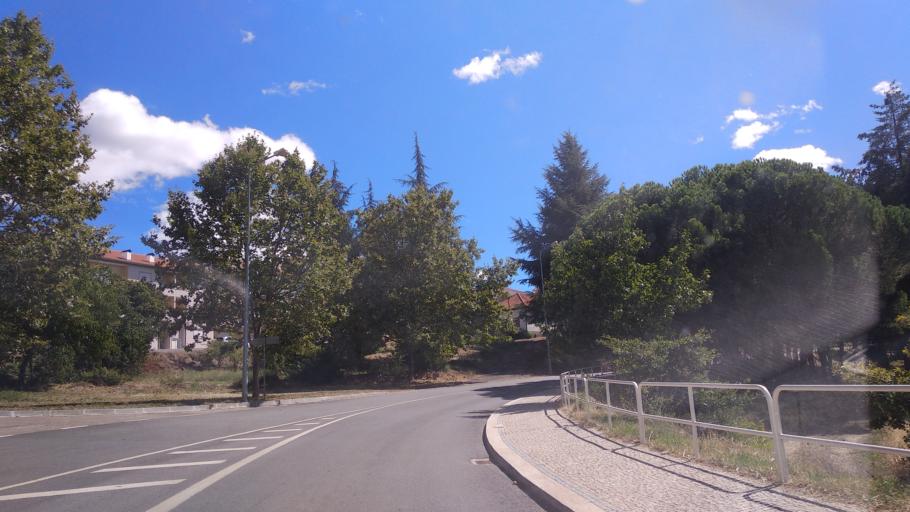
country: PT
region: Braganca
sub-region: Braganca Municipality
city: Braganca
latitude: 41.7981
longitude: -6.7604
